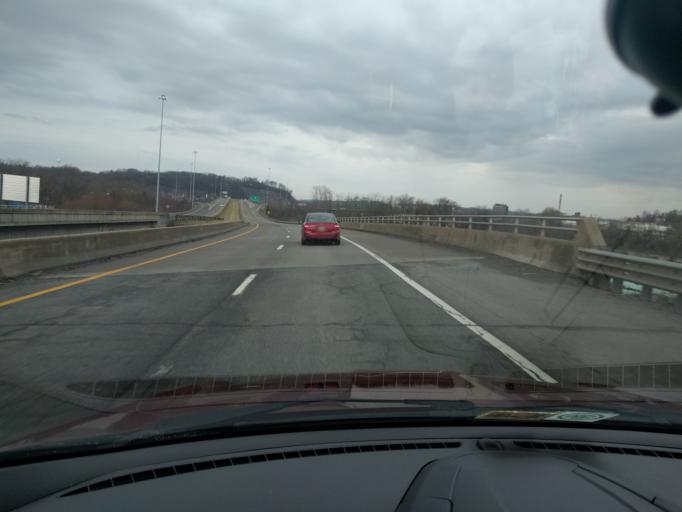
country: US
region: West Virginia
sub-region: Wood County
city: Parkersburg
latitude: 39.2563
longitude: -81.5475
